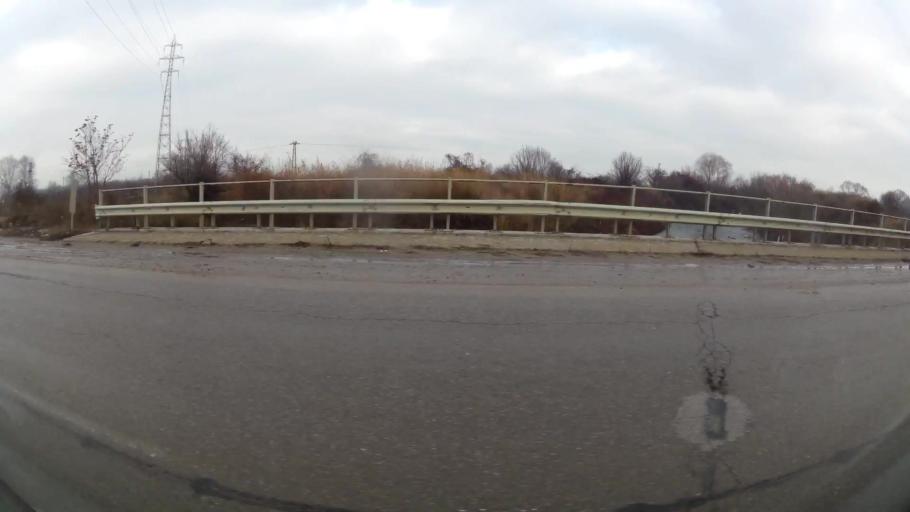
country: BG
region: Sofia-Capital
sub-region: Stolichna Obshtina
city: Sofia
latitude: 42.7223
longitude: 23.3669
